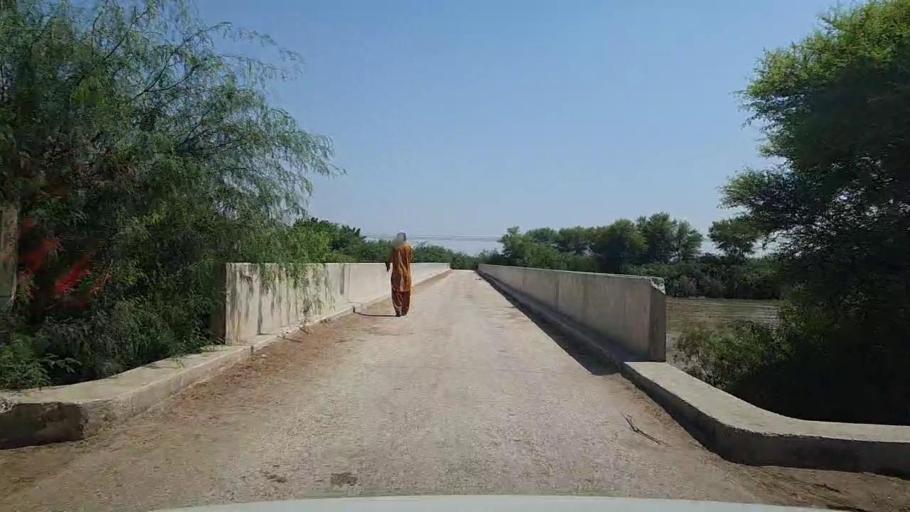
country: PK
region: Sindh
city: Kandhkot
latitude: 28.2880
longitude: 69.3537
